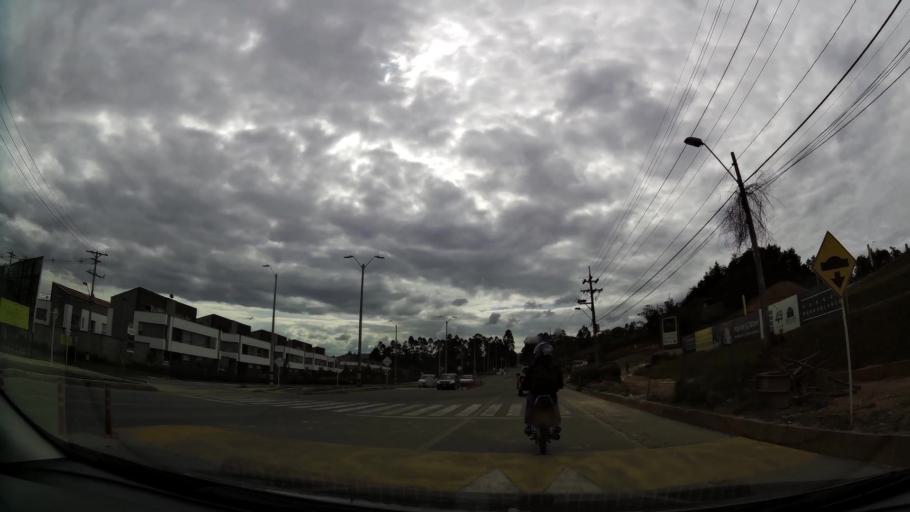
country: CO
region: Antioquia
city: Rionegro
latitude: 6.1518
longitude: -75.3973
